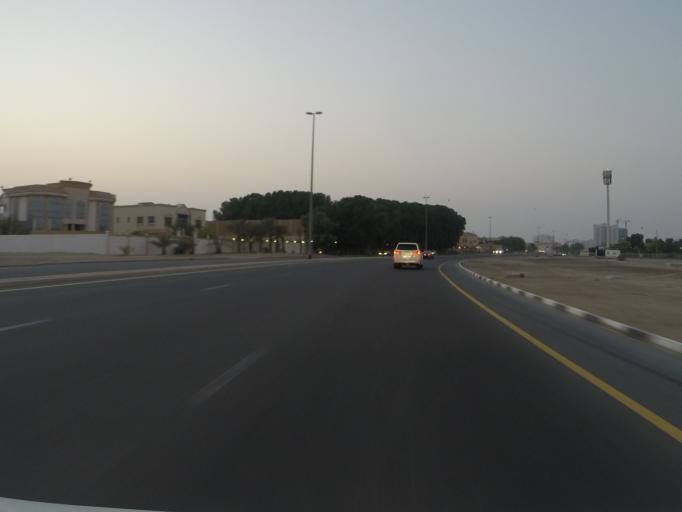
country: AE
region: Dubai
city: Dubai
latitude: 25.0980
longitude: 55.2005
